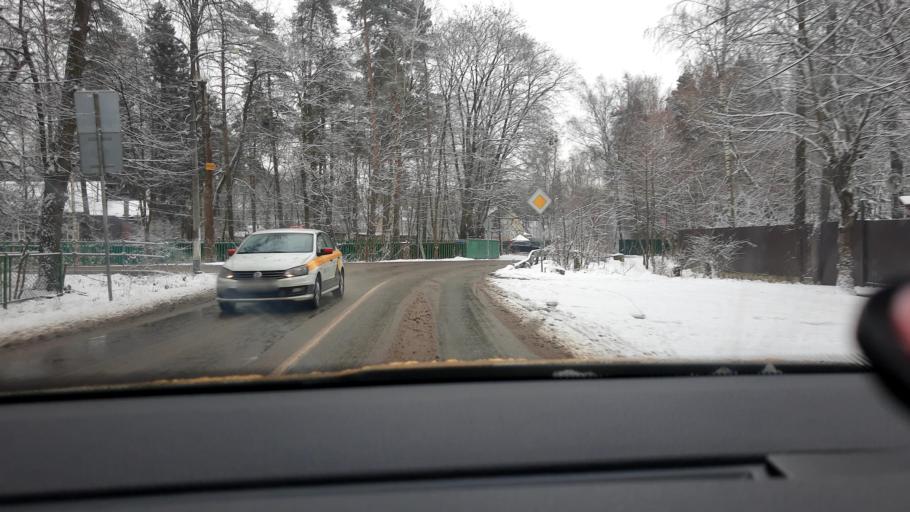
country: RU
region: Moskovskaya
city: Mamontovka
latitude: 55.9752
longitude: 37.8216
